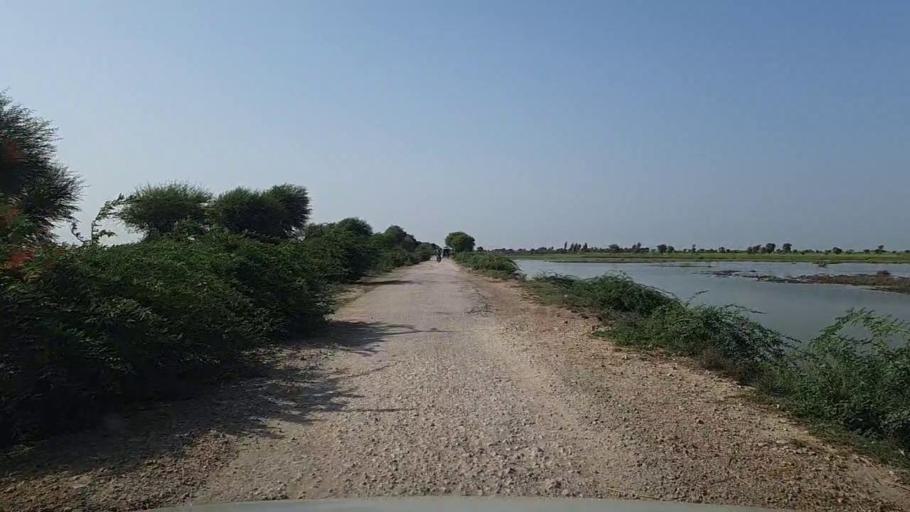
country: PK
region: Sindh
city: Kario
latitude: 24.7971
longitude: 68.5571
